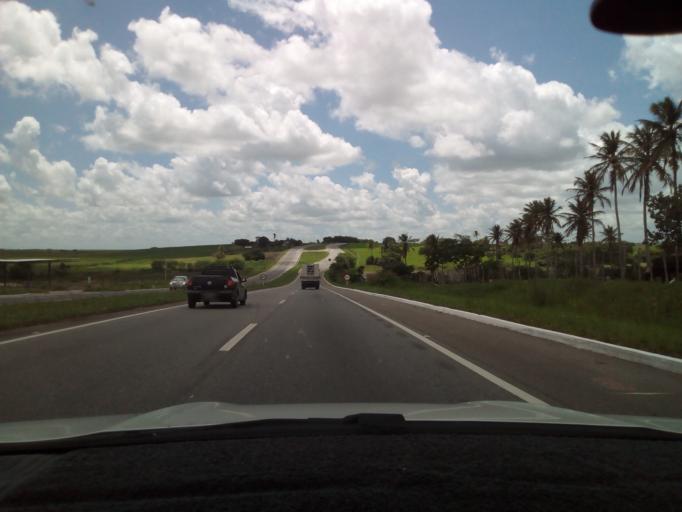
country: BR
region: Paraiba
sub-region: Pilar
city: Pilar
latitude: -7.1903
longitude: -35.2185
